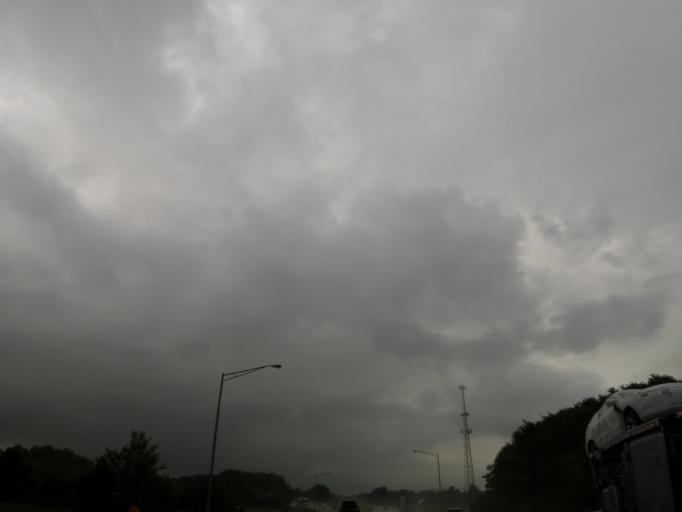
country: US
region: Illinois
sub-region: Jefferson County
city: Mount Vernon
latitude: 38.3313
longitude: -88.9550
